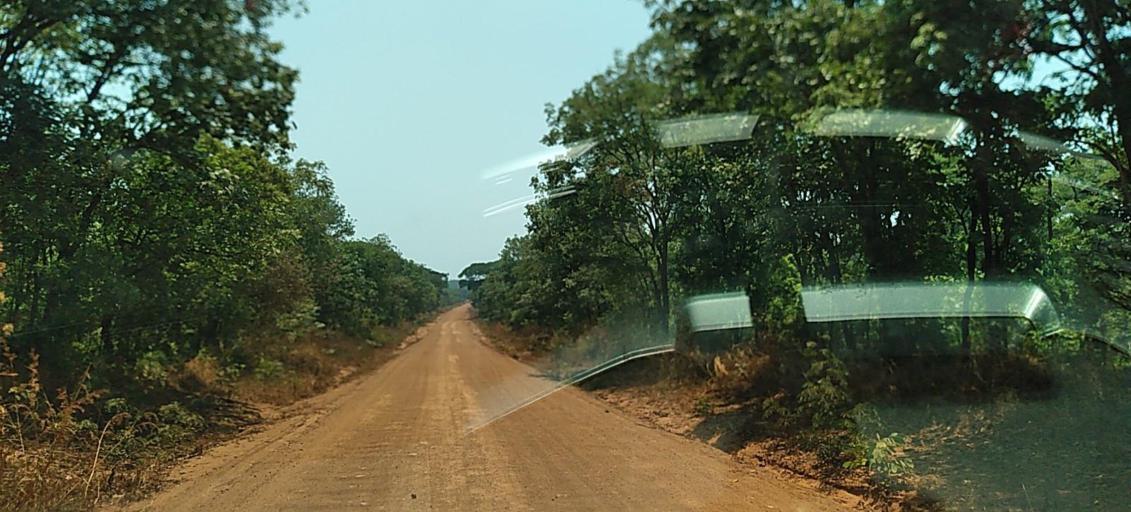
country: ZM
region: North-Western
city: Kansanshi
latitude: -11.9890
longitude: 26.8430
